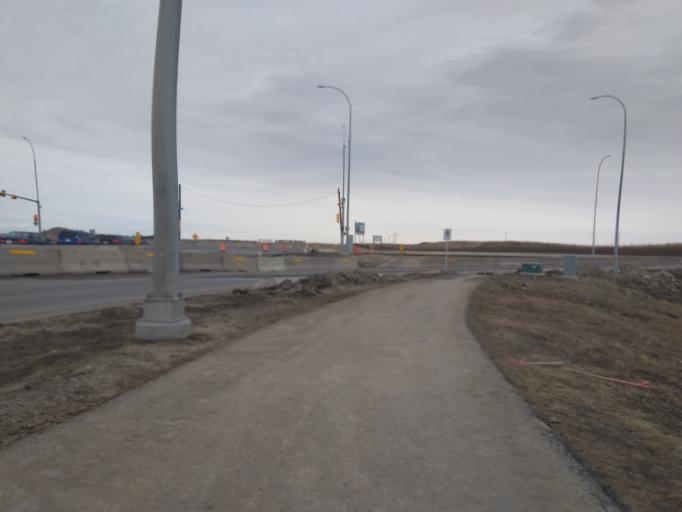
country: CA
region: Alberta
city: Calgary
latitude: 51.1390
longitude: -113.9465
